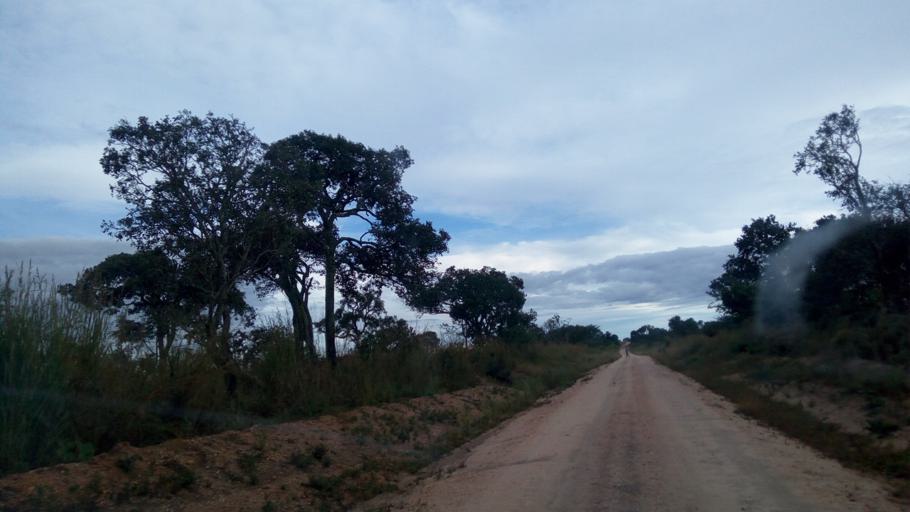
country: CD
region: Katanga
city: Kalemie
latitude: -6.5916
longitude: 29.0392
